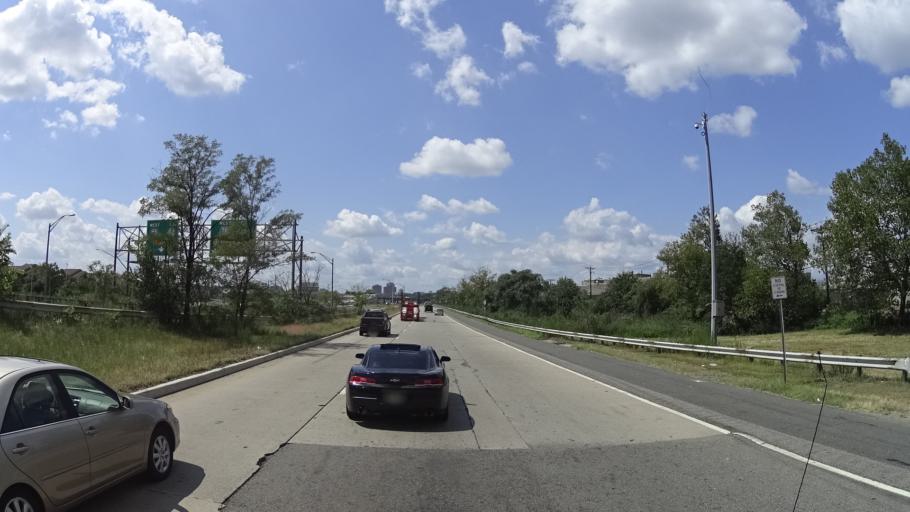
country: US
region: New Jersey
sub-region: Essex County
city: Newark
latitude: 40.7115
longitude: -74.1700
